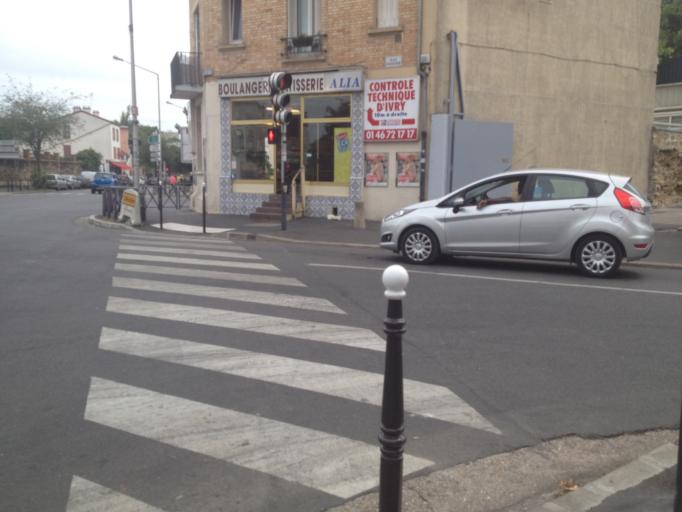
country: FR
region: Ile-de-France
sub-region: Departement du Val-de-Marne
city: Ivry-sur-Seine
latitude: 48.8108
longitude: 2.3801
